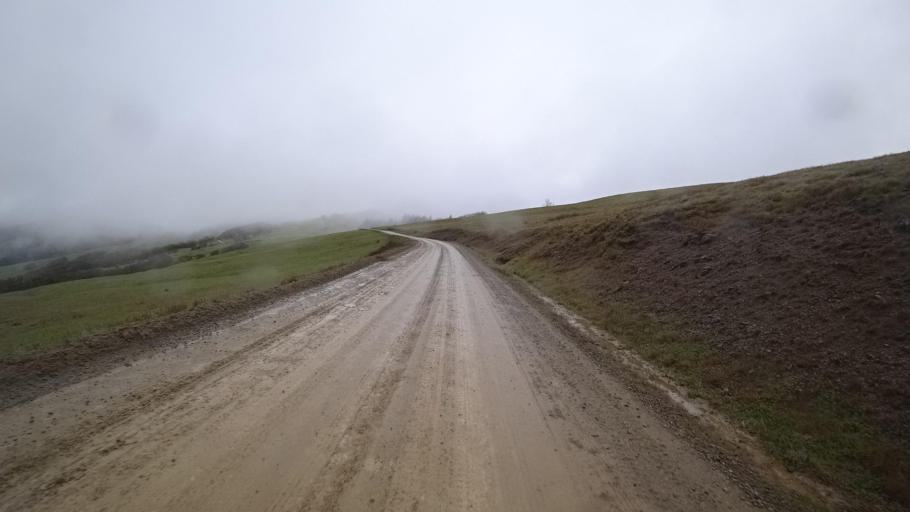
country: US
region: California
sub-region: Humboldt County
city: Westhaven-Moonstone
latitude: 41.1460
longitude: -123.8698
